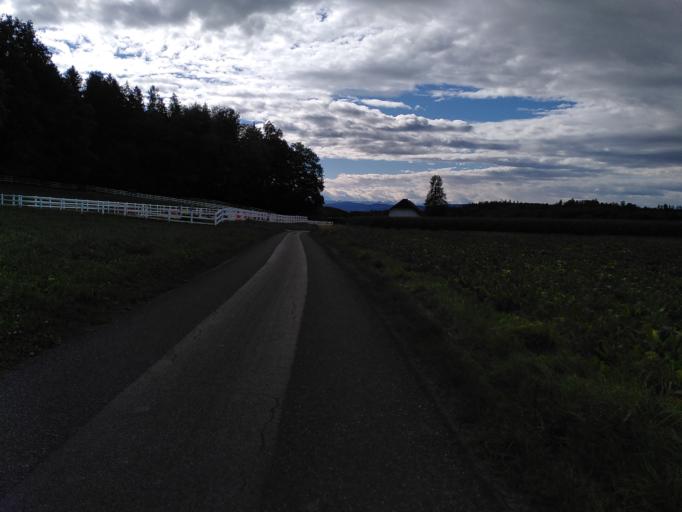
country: CH
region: Bern
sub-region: Emmental District
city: Ersigen
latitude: 47.0953
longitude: 7.6070
